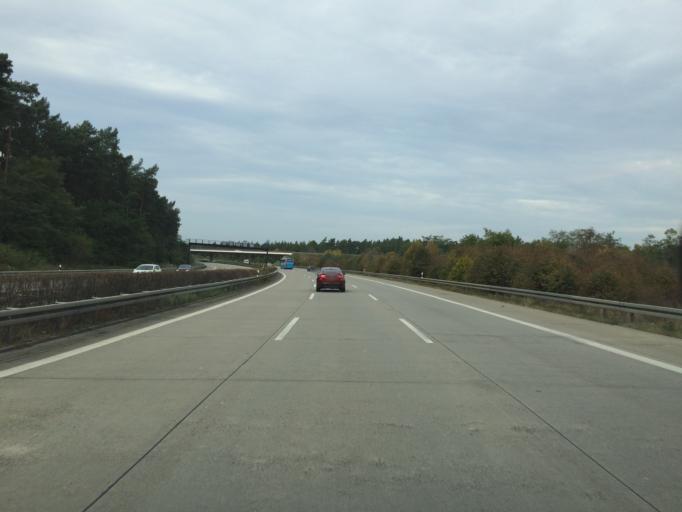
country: DE
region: Brandenburg
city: Gross Kreutz
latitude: 52.3350
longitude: 12.8147
